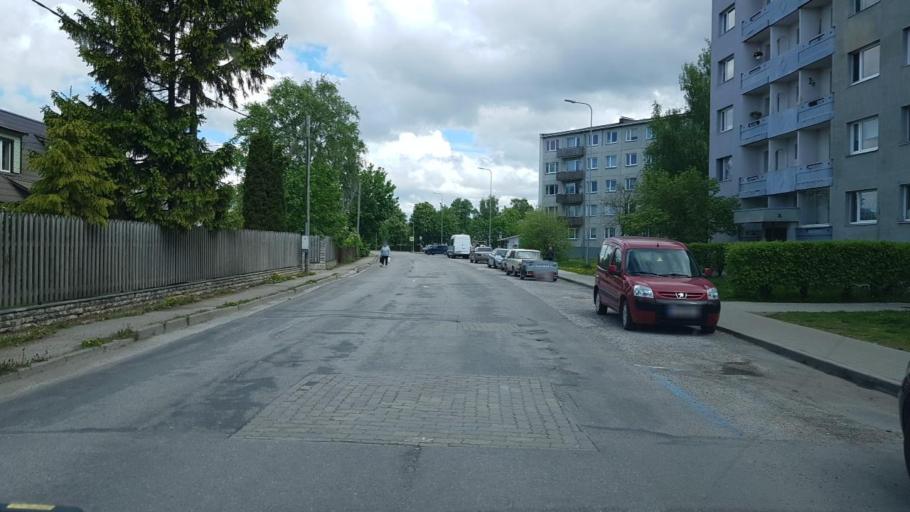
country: EE
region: Laeaene
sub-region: Haapsalu linn
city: Haapsalu
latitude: 58.9352
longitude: 23.5505
